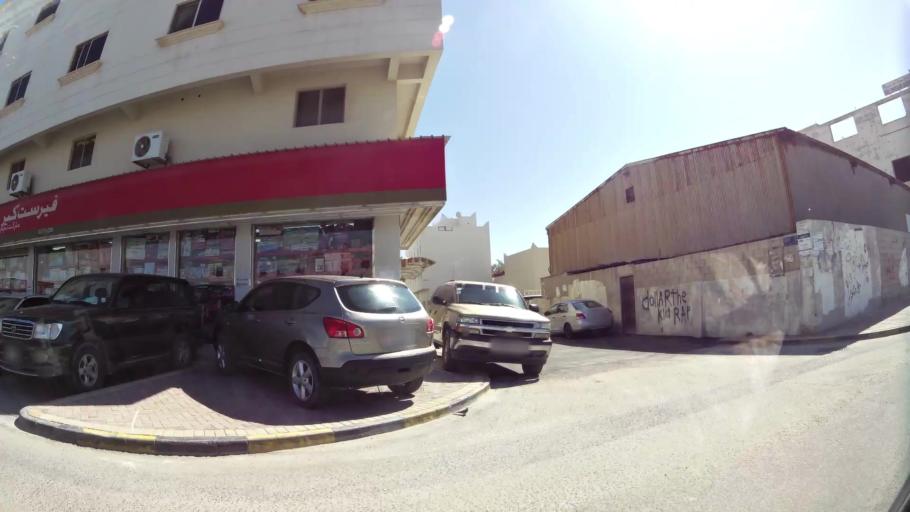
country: BH
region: Muharraq
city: Al Muharraq
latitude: 26.2447
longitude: 50.6128
